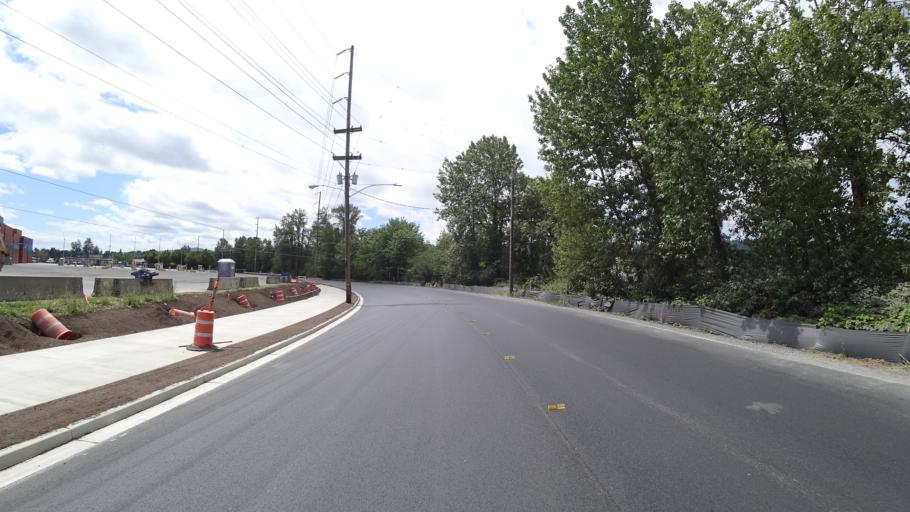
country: US
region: Oregon
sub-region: Washington County
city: West Haven
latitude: 45.6107
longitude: -122.7682
